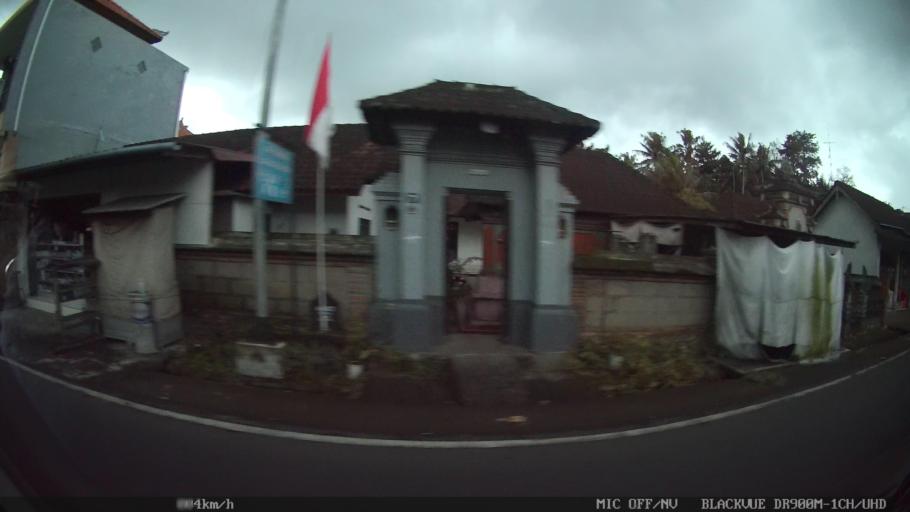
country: ID
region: Bali
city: Banjar Keraman
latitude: -8.5304
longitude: 115.2268
